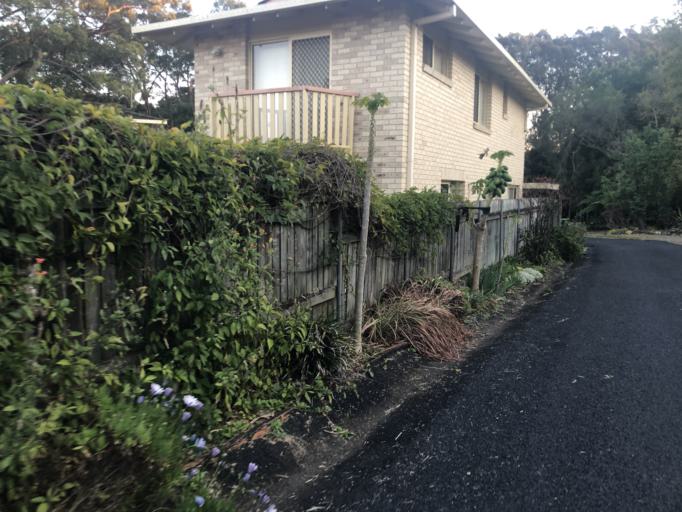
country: AU
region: New South Wales
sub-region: Coffs Harbour
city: Coffs Harbour
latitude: -30.2989
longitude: 153.1212
